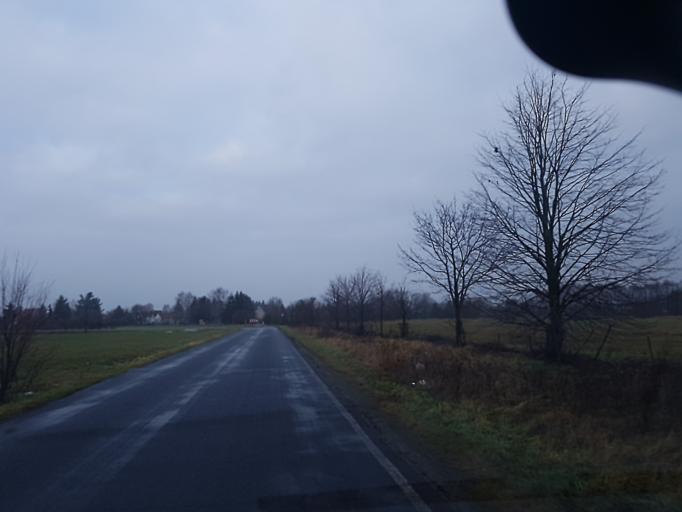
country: DE
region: Brandenburg
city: Finsterwalde
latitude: 51.6073
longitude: 13.7193
